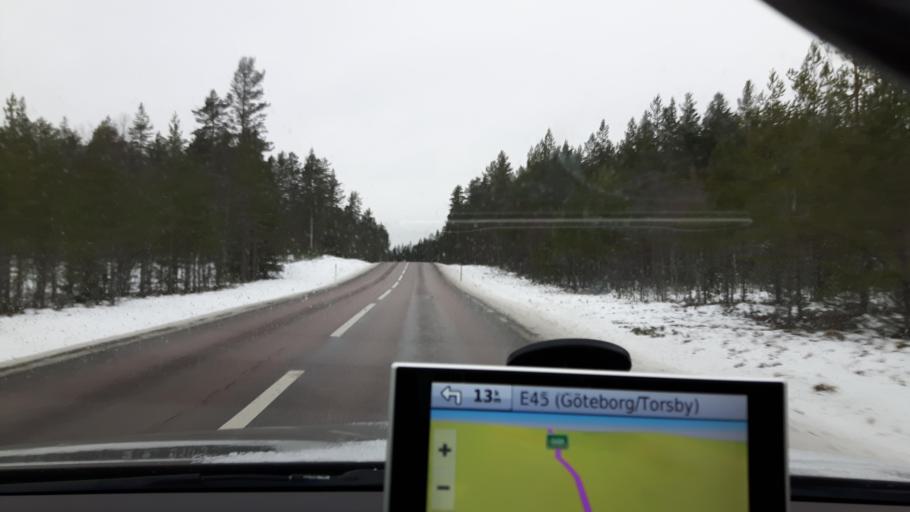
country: SE
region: Vaermland
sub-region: Torsby Kommun
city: Torsby
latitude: 60.3665
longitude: 13.1954
